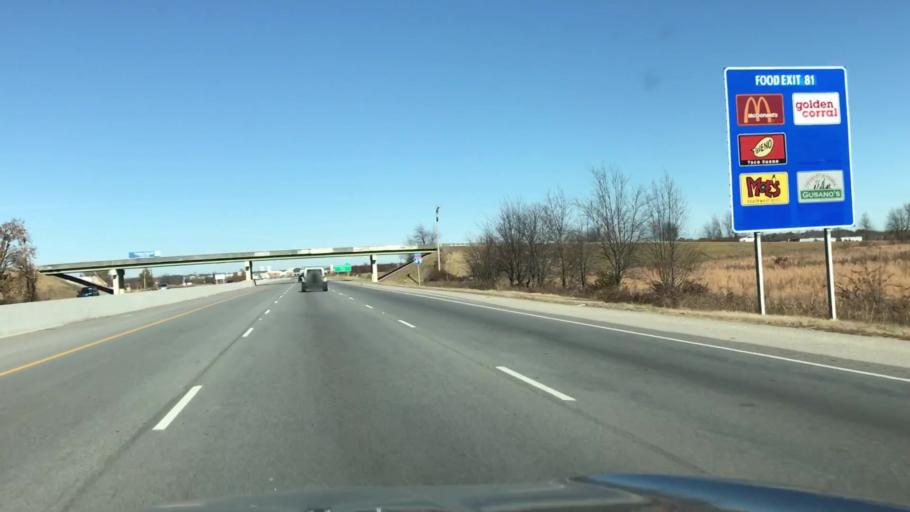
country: US
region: Arkansas
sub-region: Benton County
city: Lowell
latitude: 36.2639
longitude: -94.1502
